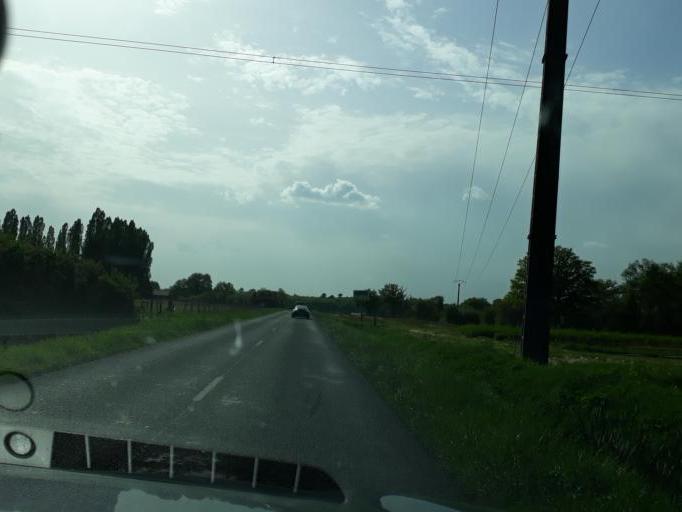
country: FR
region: Centre
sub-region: Departement du Loir-et-Cher
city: Saint-Laurent-Nouan
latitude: 47.6575
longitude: 1.6413
